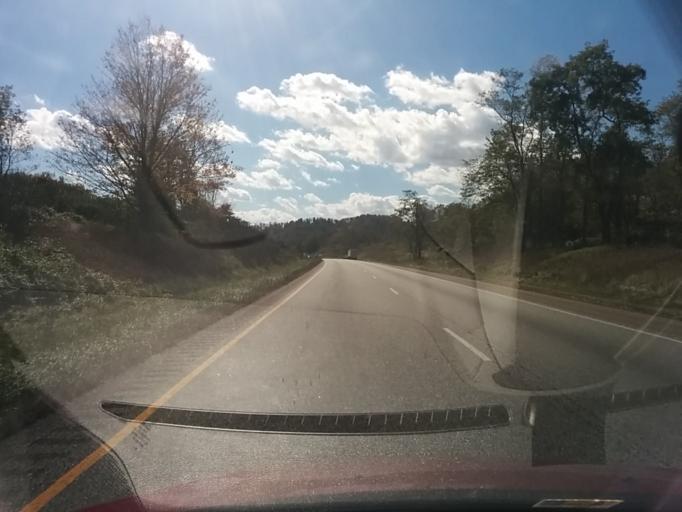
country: US
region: Virginia
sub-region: Augusta County
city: Stuarts Draft
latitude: 38.0097
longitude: -79.1659
